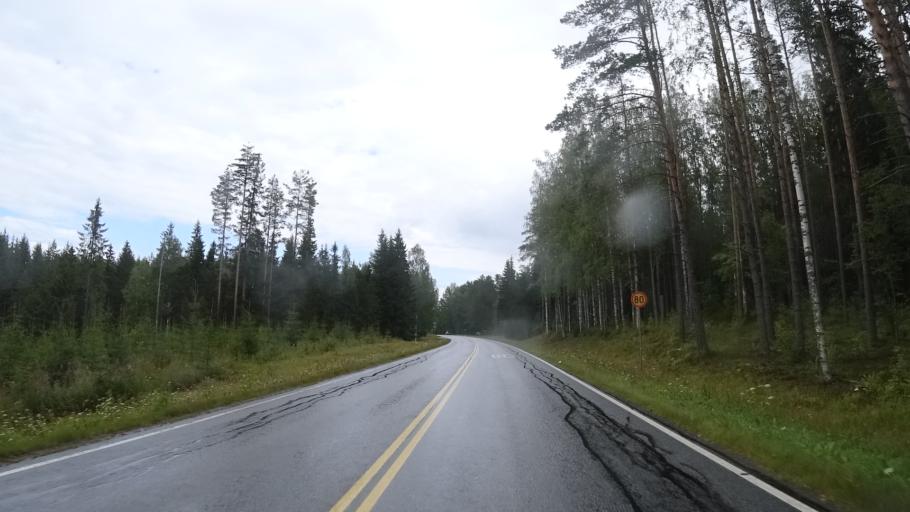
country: FI
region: North Karelia
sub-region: Keski-Karjala
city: Raeaekkylae
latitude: 62.0768
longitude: 29.6470
